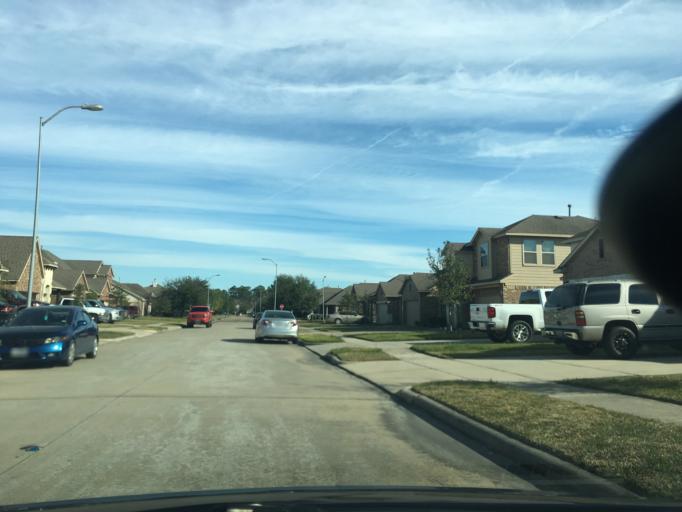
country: US
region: Texas
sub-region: Harris County
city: Cloverleaf
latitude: 29.8155
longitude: -95.1594
